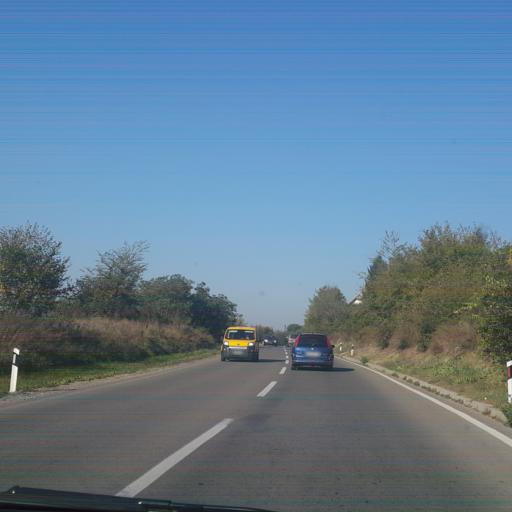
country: RS
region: Central Serbia
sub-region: Toplicki Okrug
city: Prokuplje
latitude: 43.2345
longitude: 21.5200
